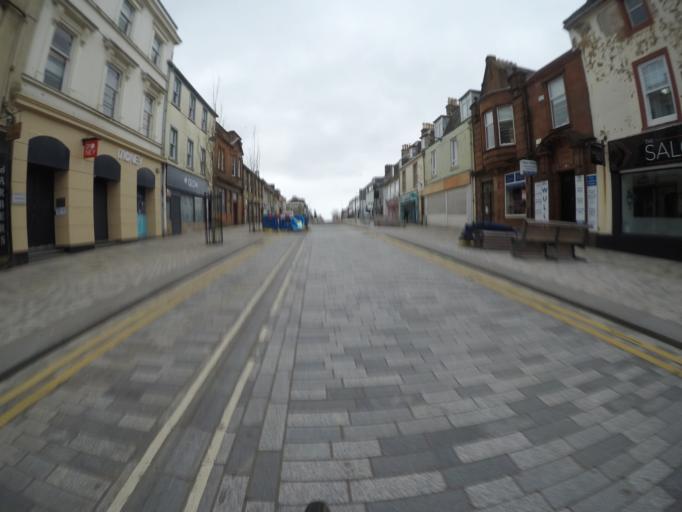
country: GB
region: Scotland
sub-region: North Ayrshire
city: Irvine
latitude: 55.6154
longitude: -4.6678
